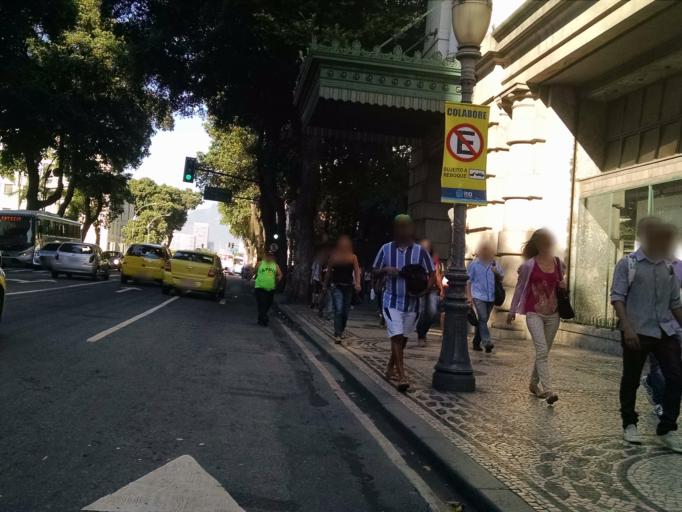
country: BR
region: Rio de Janeiro
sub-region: Rio De Janeiro
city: Rio de Janeiro
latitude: -22.9024
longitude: -43.1860
